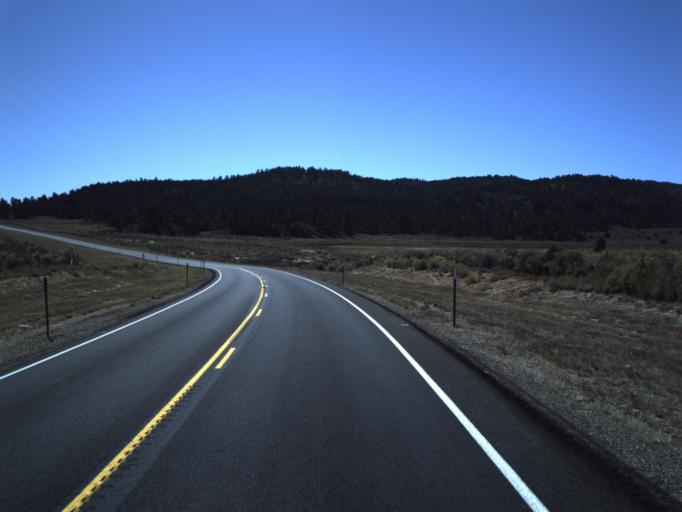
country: US
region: Utah
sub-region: Garfield County
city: Panguitch
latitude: 37.6740
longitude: -111.8272
